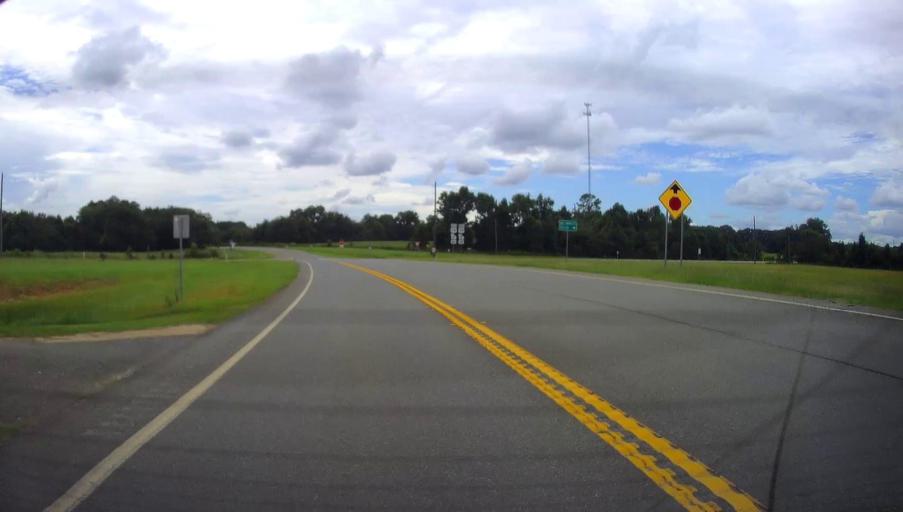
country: US
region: Georgia
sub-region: Schley County
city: Ellaville
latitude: 32.2240
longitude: -84.2852
